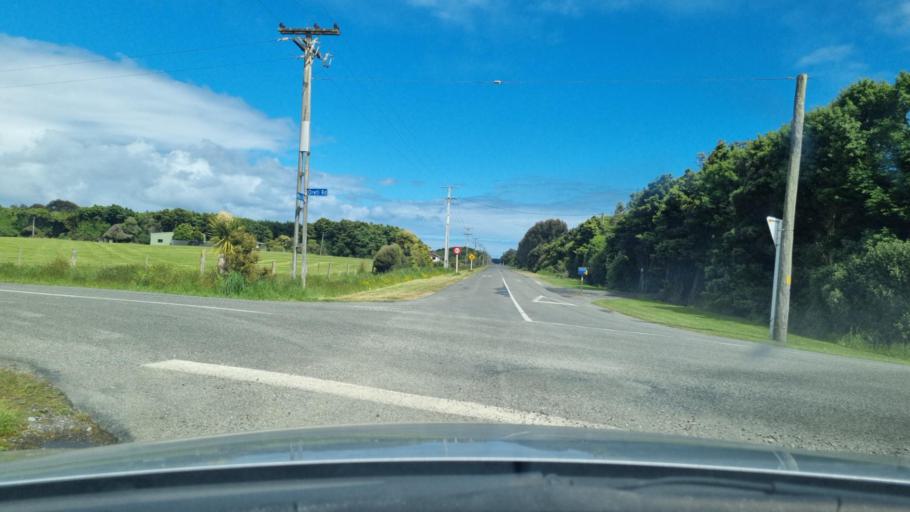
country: NZ
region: Southland
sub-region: Invercargill City
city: Invercargill
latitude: -46.4416
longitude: 168.2907
